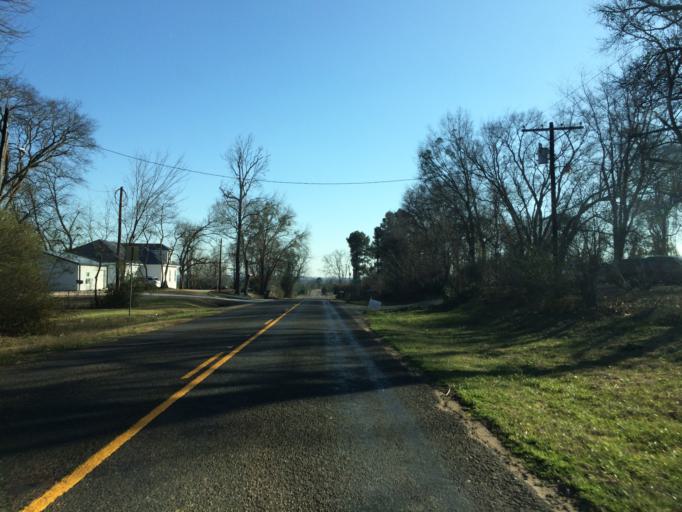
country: US
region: Texas
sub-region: Wood County
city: Hawkins
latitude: 32.6195
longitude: -95.3132
